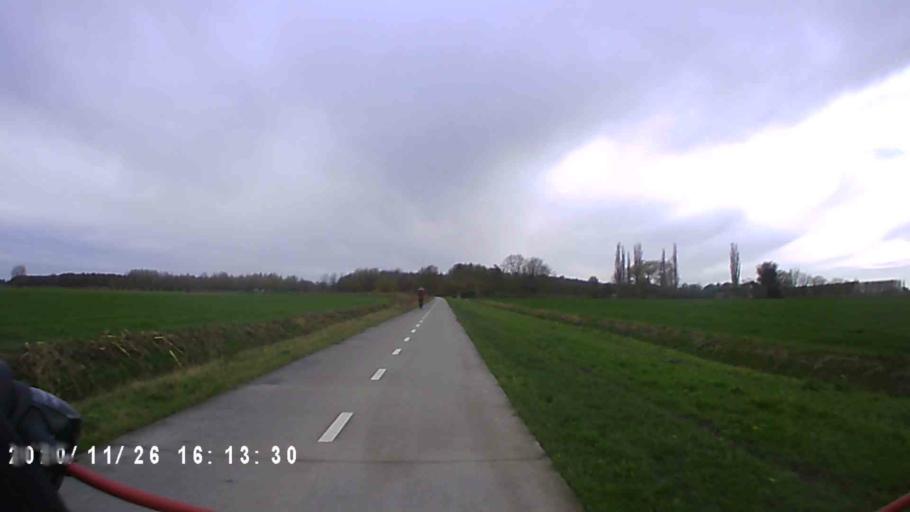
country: NL
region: Groningen
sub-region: Gemeente Groningen
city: Oosterpark
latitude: 53.2470
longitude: 6.6418
